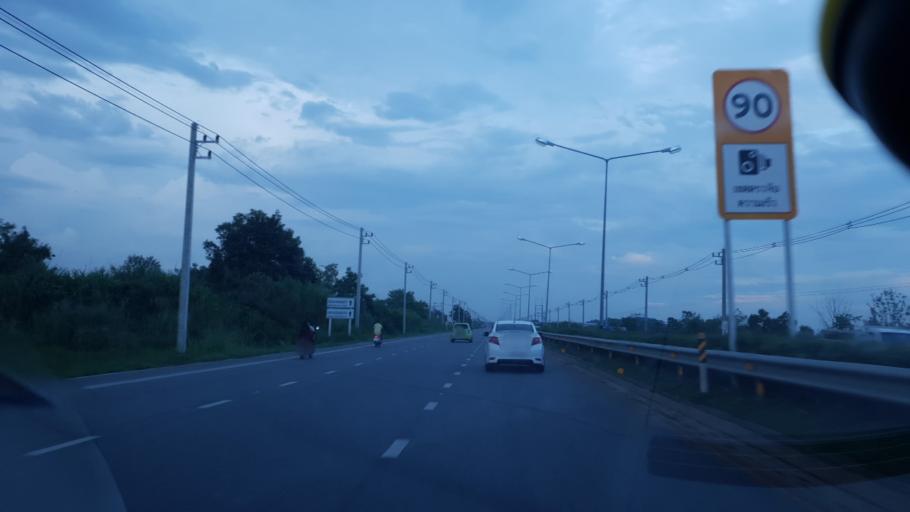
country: TH
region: Chiang Rai
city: Chiang Rai
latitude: 19.8746
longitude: 99.8477
